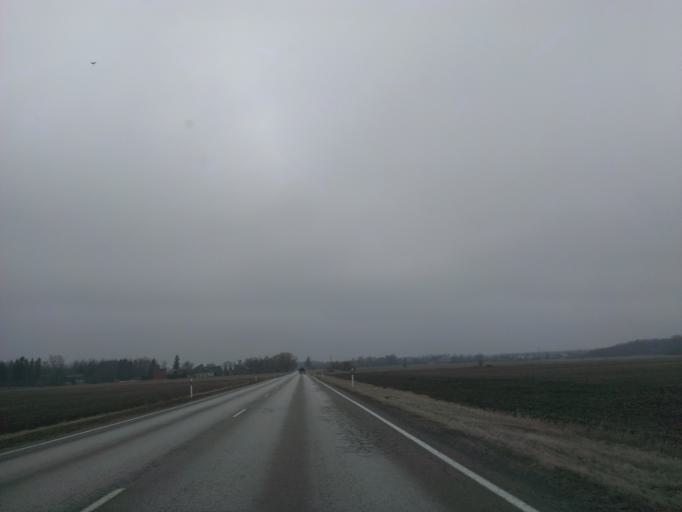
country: EE
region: Paernumaa
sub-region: Audru vald
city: Audru
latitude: 58.4673
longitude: 24.2051
